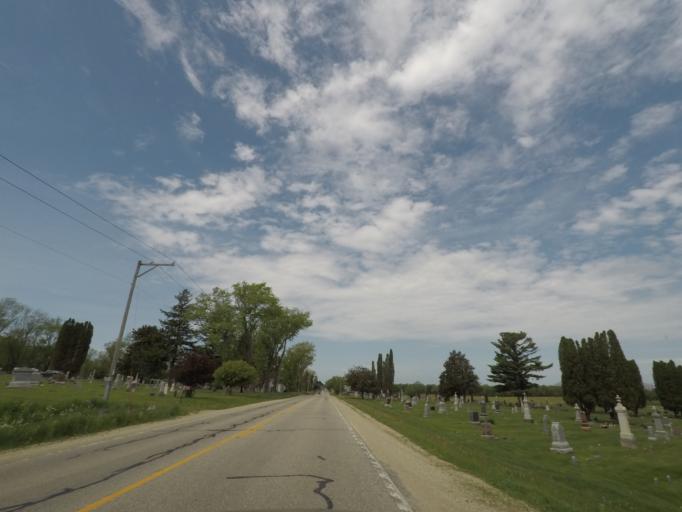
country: US
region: Wisconsin
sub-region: Rock County
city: Orfordville
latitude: 42.6217
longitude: -89.2440
